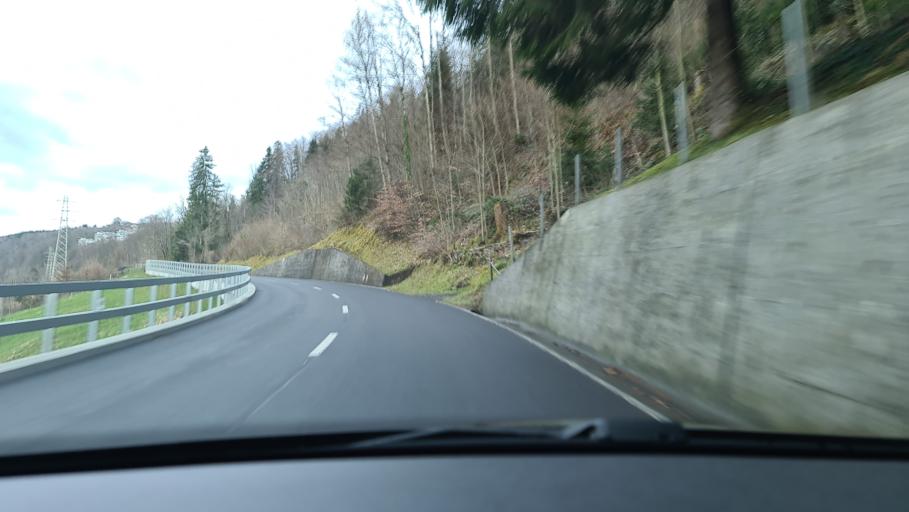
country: CH
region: Nidwalden
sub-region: Nidwalden
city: Beckenried
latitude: 46.9596
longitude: 8.4942
